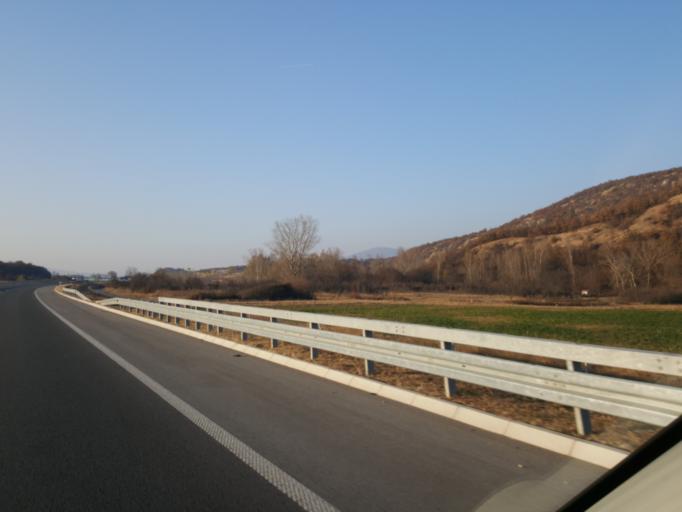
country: RS
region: Central Serbia
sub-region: Pirotski Okrug
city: Dimitrovgrad
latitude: 43.0486
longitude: 22.7030
